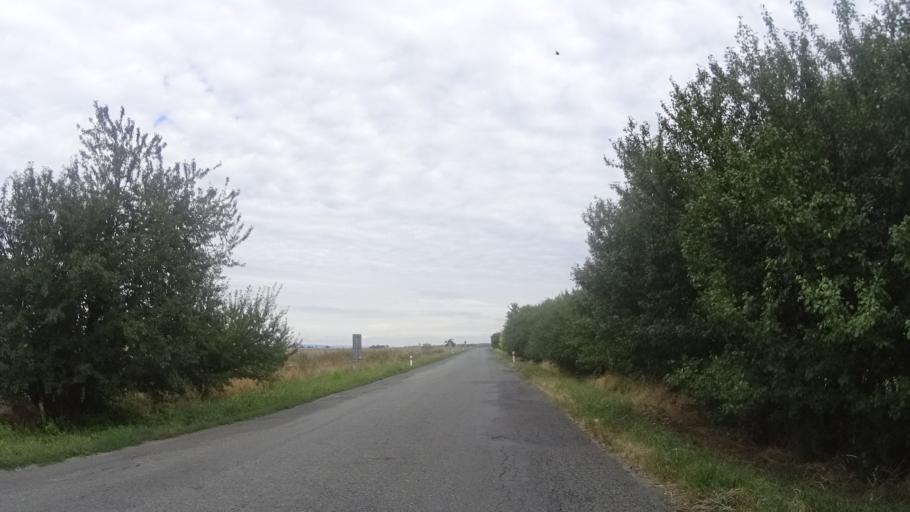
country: CZ
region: Olomoucky
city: Tovacov
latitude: 49.4053
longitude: 17.2857
